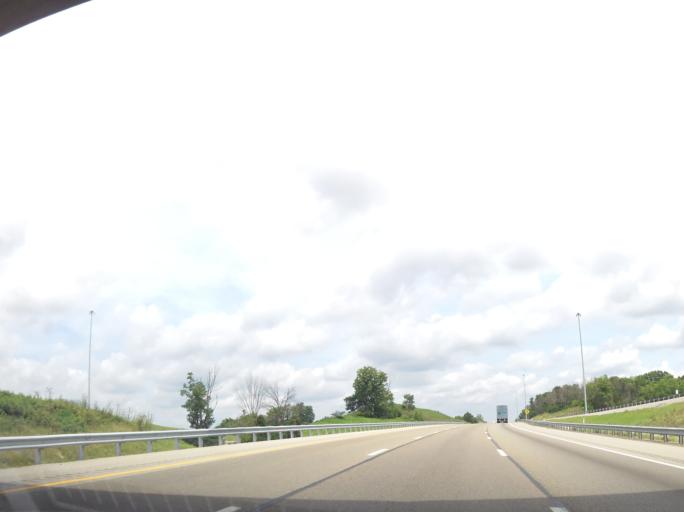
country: US
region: Kentucky
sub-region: Grant County
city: Williamstown
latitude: 38.4901
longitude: -84.5861
